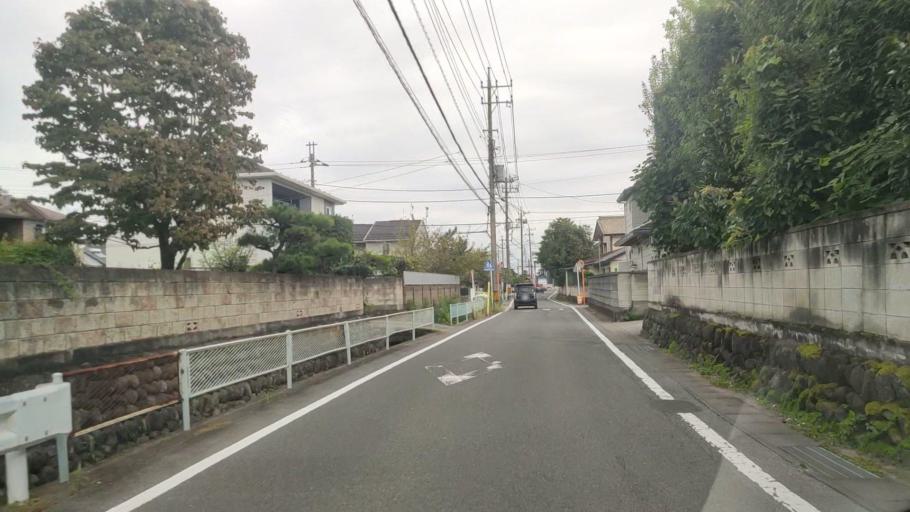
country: JP
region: Gunma
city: Takasaki
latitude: 36.3585
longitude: 138.9991
